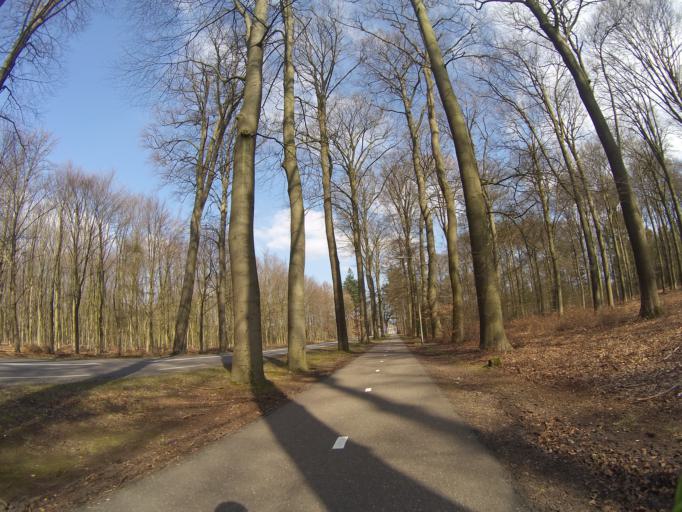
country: NL
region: Utrecht
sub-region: Gemeente Soest
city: Soest
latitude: 52.1810
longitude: 5.2579
